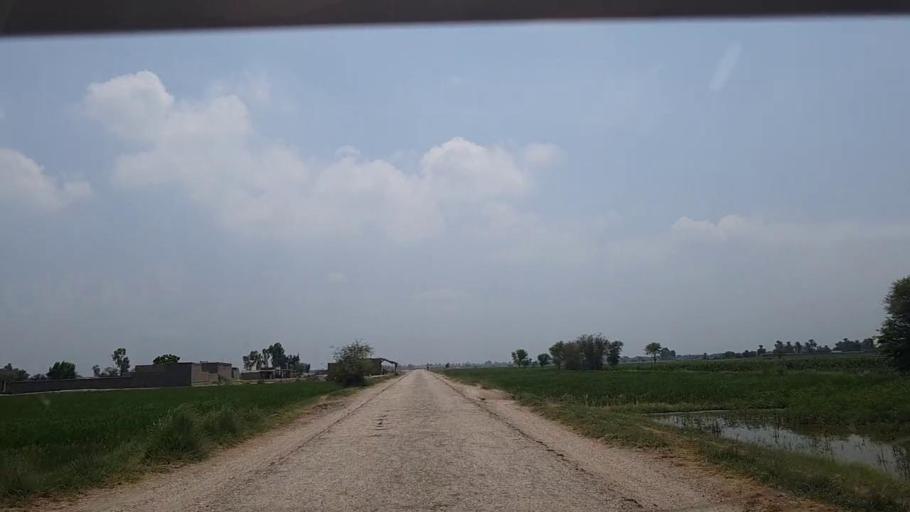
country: PK
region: Sindh
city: Khanpur
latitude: 27.9041
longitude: 69.3916
